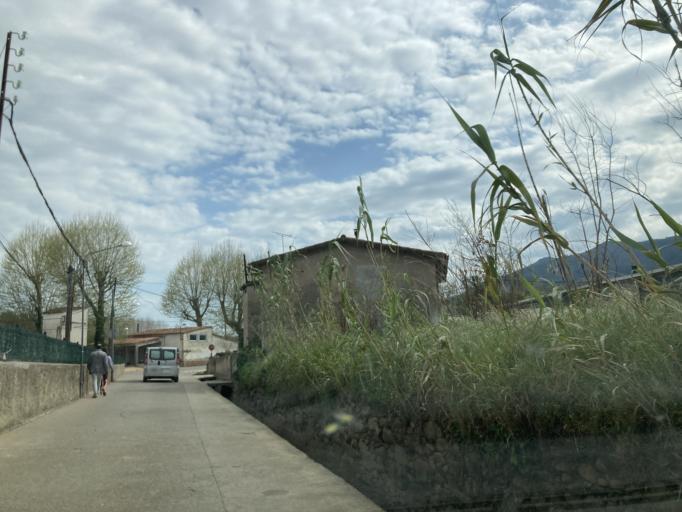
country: ES
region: Catalonia
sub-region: Provincia de Girona
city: la Cellera de Ter
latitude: 41.9669
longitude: 2.6209
